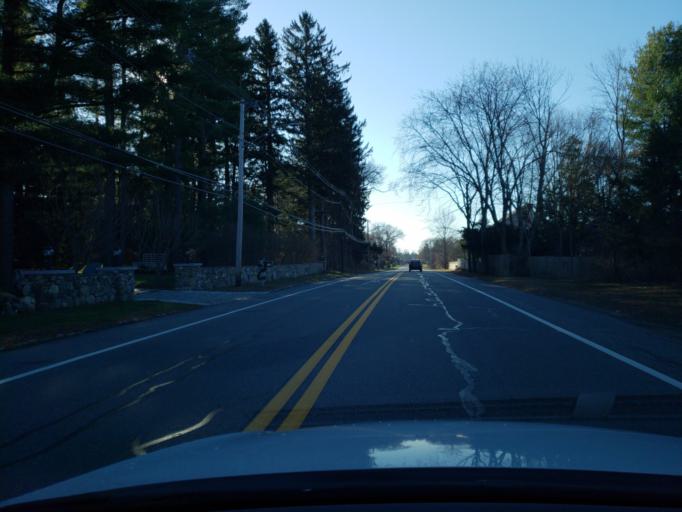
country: US
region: Massachusetts
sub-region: Essex County
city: Andover
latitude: 42.6315
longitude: -71.1278
